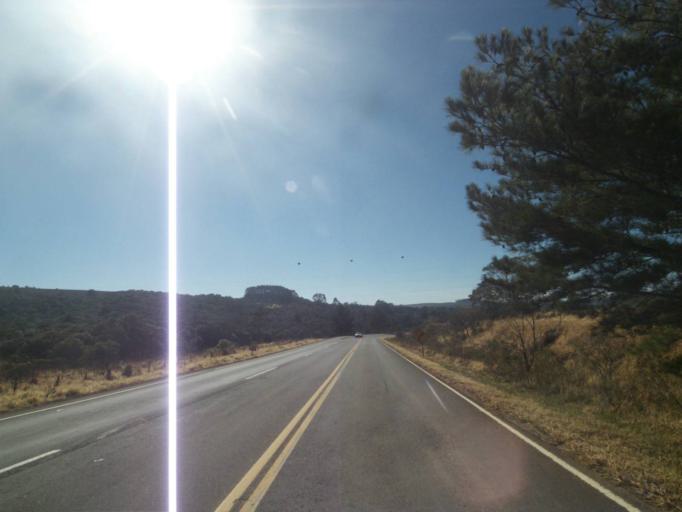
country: BR
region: Parana
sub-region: Tibagi
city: Tibagi
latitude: -24.4701
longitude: -50.5033
